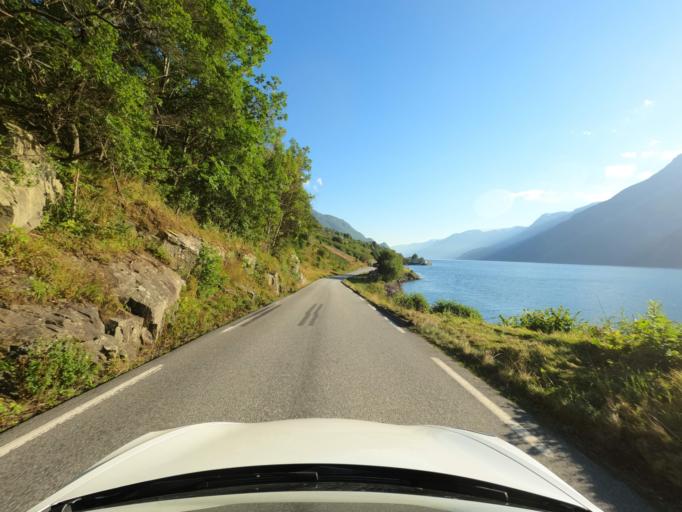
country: NO
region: Hordaland
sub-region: Ullensvang
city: Kinsarvik
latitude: 60.3487
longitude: 6.6608
